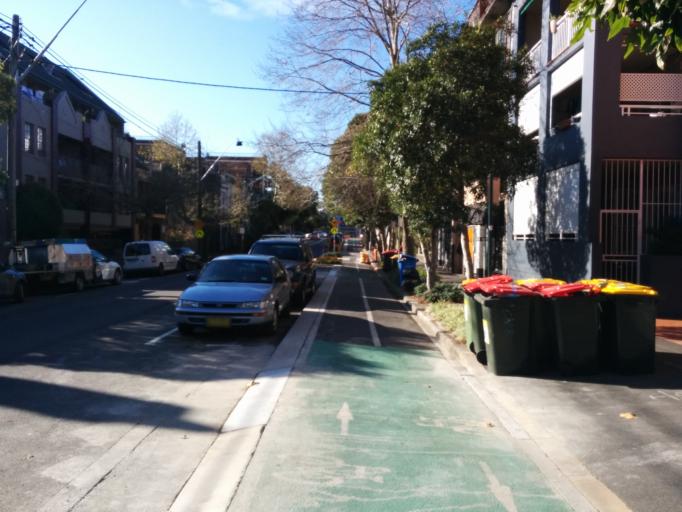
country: AU
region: New South Wales
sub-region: City of Sydney
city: Redfern
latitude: -33.8905
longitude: 151.2027
